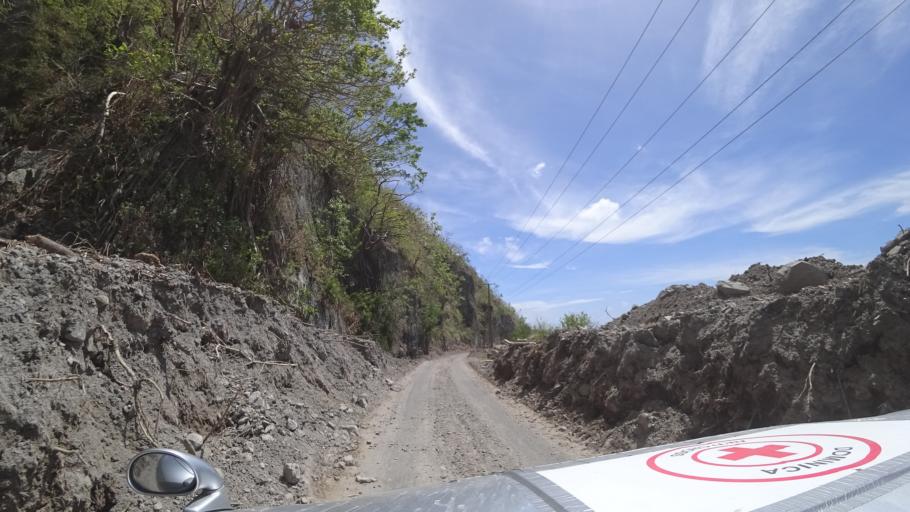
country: DM
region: Saint Luke
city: Pointe Michel
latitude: 15.2558
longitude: -61.3758
